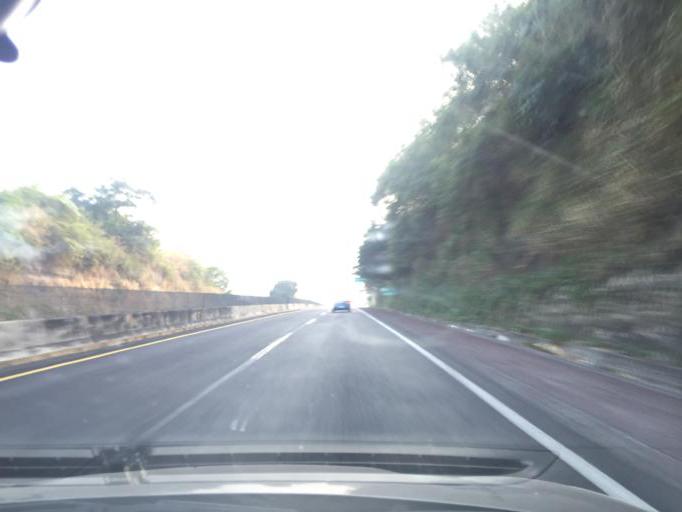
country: MX
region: Veracruz
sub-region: Tierra Blanca
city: Huixcolotla
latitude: 18.7816
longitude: -96.4670
